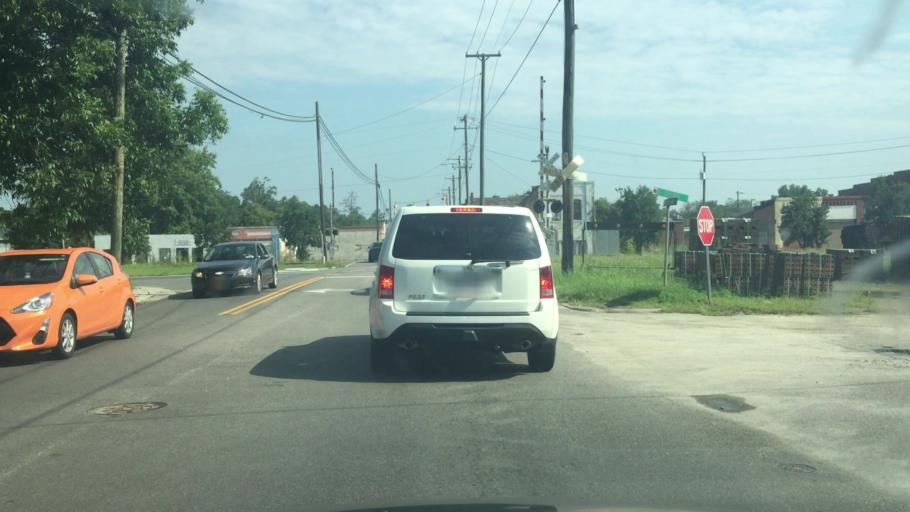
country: US
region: North Carolina
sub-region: Columbus County
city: Chadbourn
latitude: 34.3217
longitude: -78.8264
